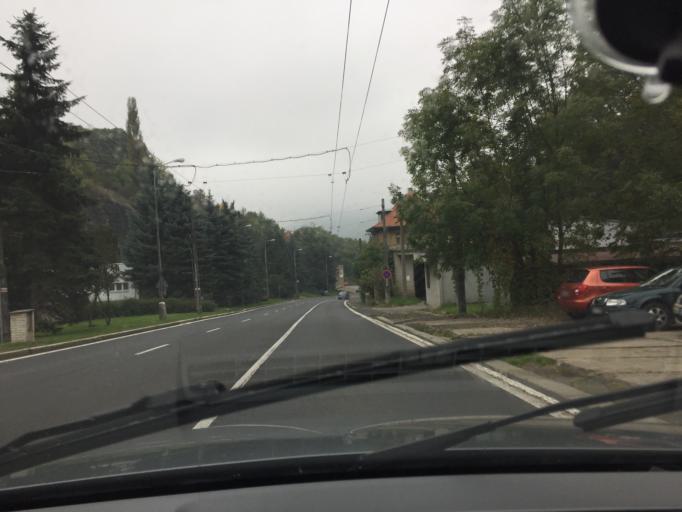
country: CZ
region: Ustecky
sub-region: Okres Usti nad Labem
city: Usti nad Labem
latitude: 50.6655
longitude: 14.0470
